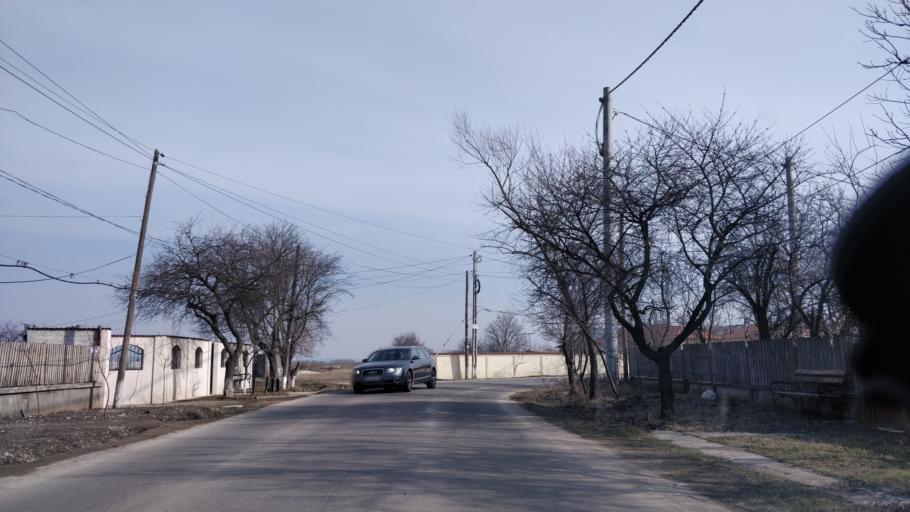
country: RO
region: Giurgiu
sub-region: Comuna Ulmi
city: Ulmi
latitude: 44.4847
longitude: 25.7925
